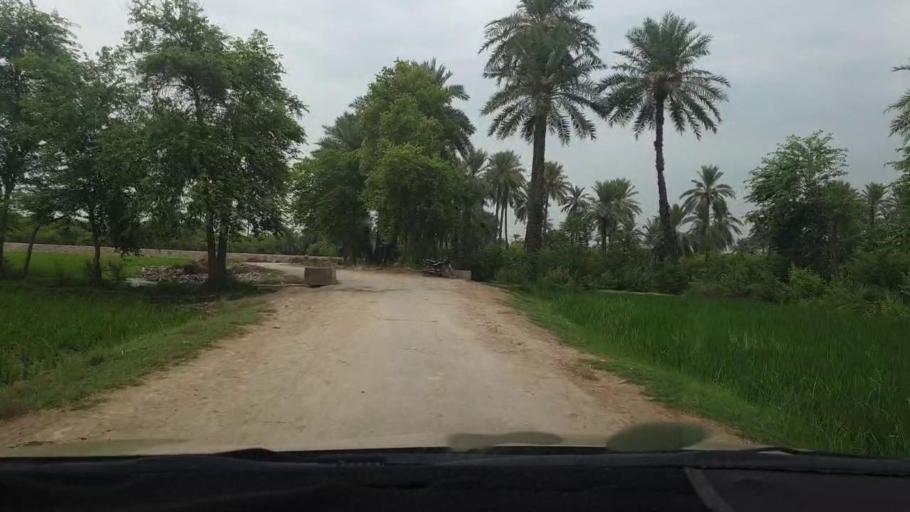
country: PK
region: Sindh
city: Larkana
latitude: 27.5725
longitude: 68.2443
